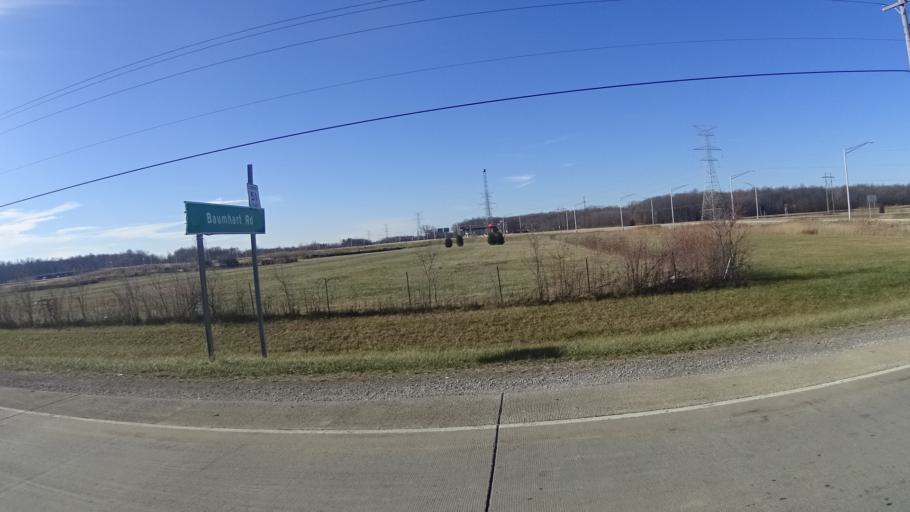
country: US
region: Ohio
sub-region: Lorain County
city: South Amherst
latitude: 41.3655
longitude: -82.2797
